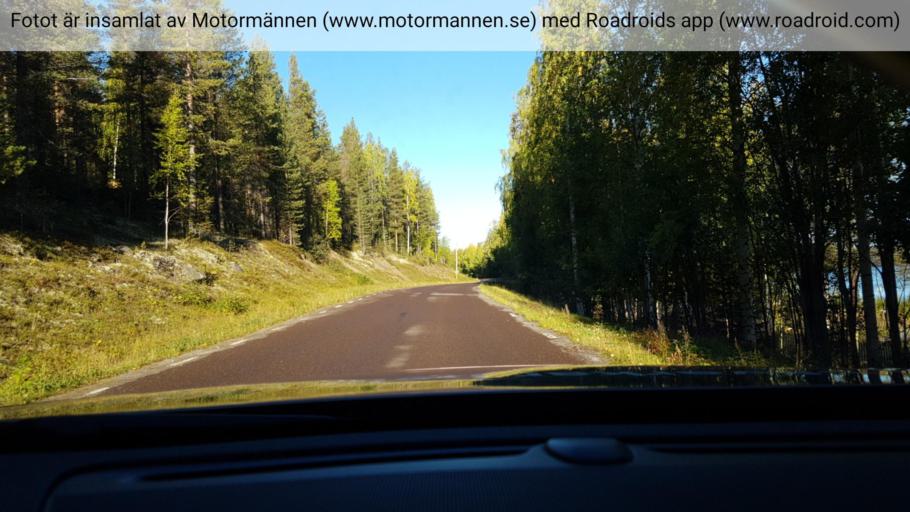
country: SE
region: Norrbotten
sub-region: Bodens Kommun
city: Boden
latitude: 66.1283
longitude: 21.3132
